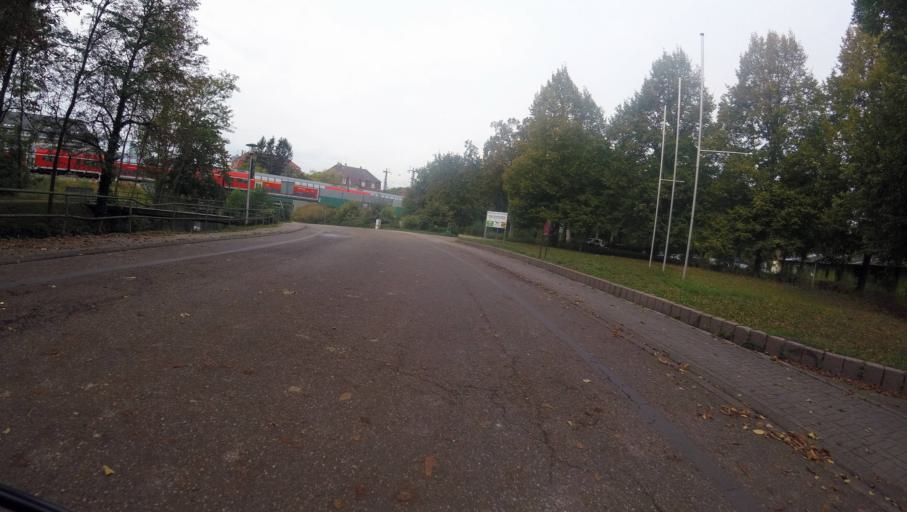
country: DE
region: Baden-Wuerttemberg
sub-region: Karlsruhe Region
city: Rastatt
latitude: 48.8538
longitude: 8.2146
